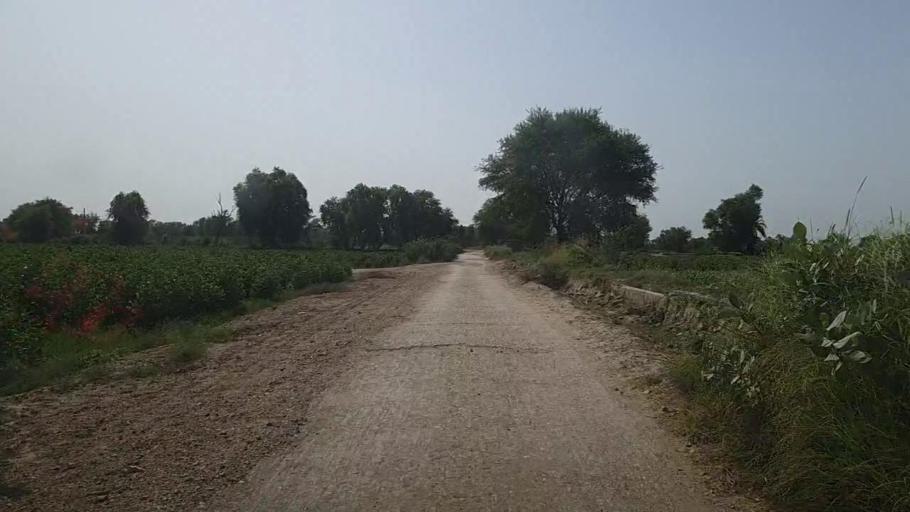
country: PK
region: Sindh
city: Pad Idan
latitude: 26.7666
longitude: 68.3224
